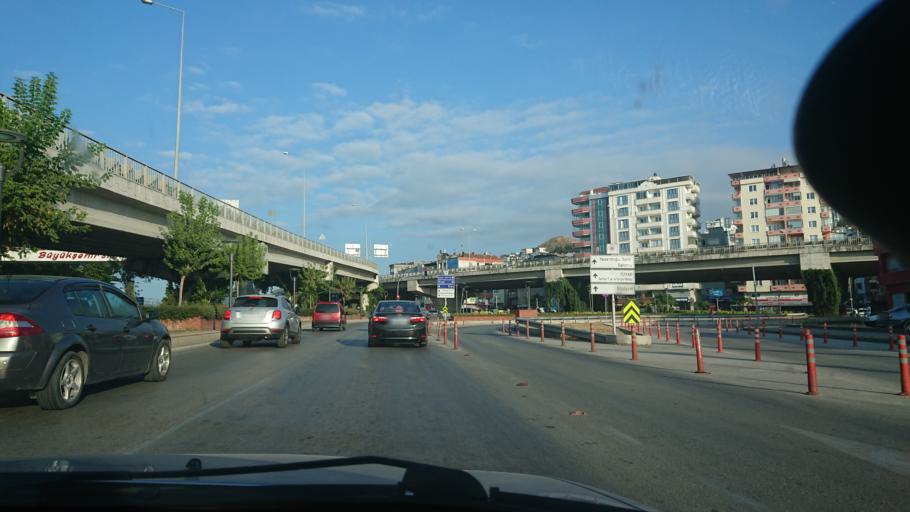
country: TR
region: Samsun
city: Samsun
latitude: 41.2729
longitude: 36.3646
